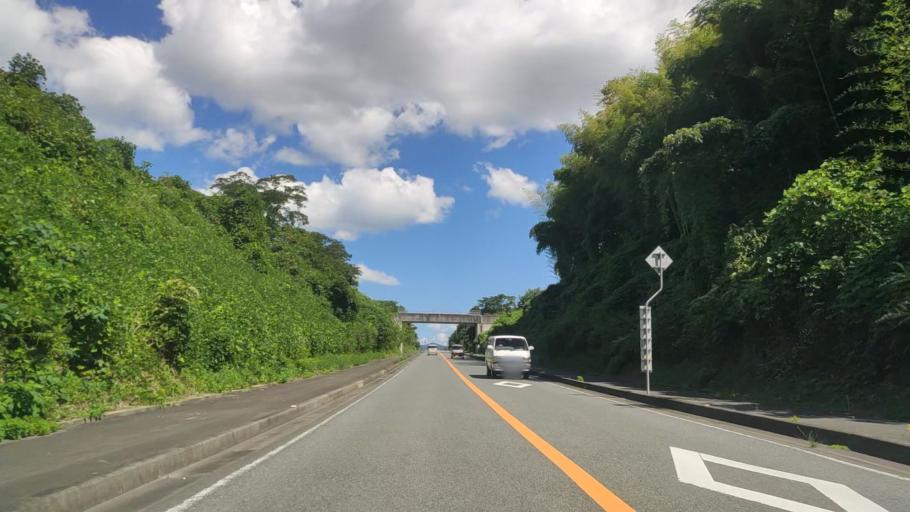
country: JP
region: Kyoto
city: Fukuchiyama
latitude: 35.2455
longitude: 135.1274
